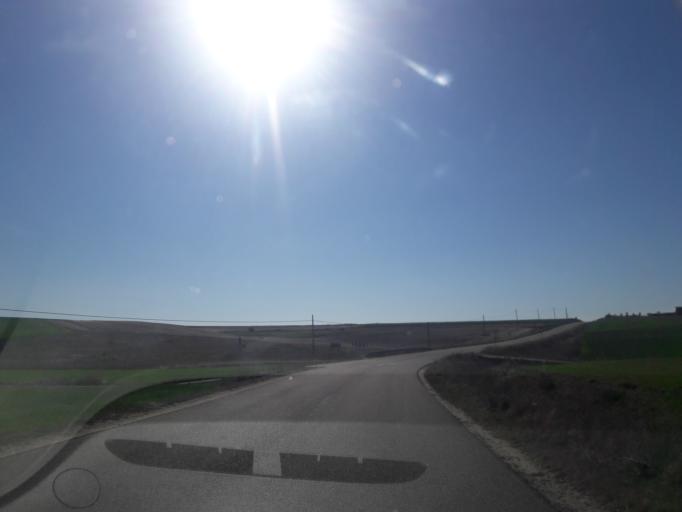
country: ES
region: Castille and Leon
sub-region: Provincia de Salamanca
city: Macotera
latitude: 40.8435
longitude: -5.3087
